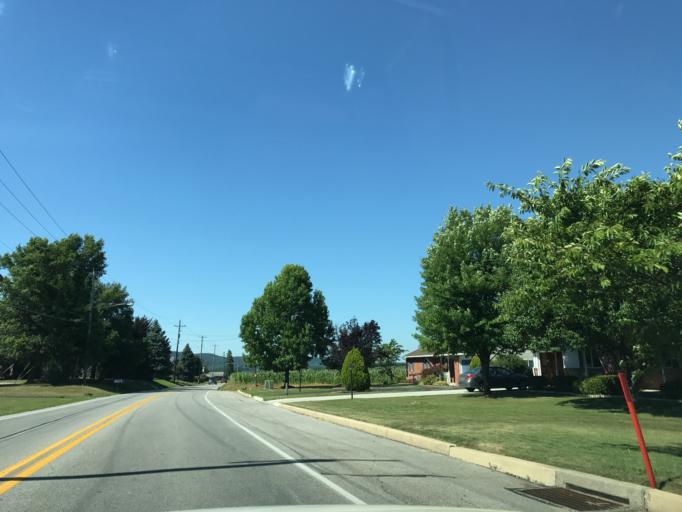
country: US
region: Pennsylvania
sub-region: York County
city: Parkville
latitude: 39.8003
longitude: -76.9455
